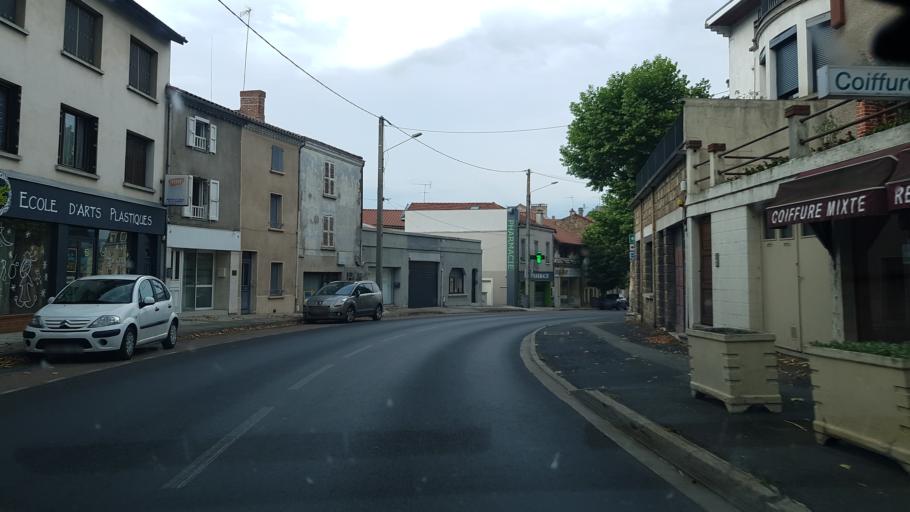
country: FR
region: Auvergne
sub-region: Departement de la Haute-Loire
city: Brioude
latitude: 45.2937
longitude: 3.3797
